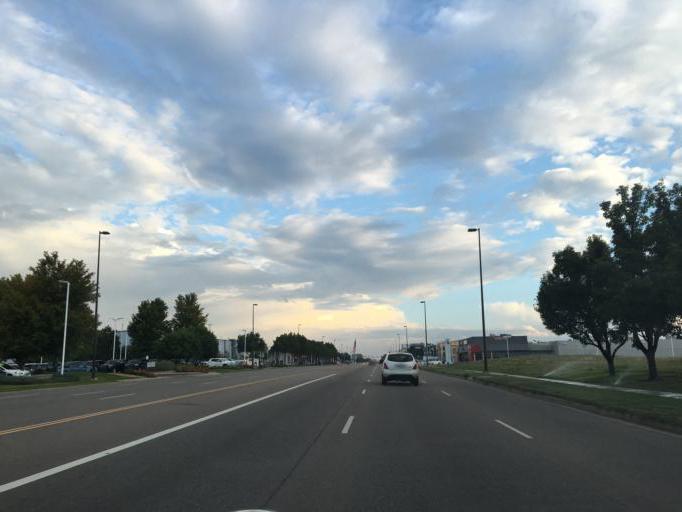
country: US
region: Colorado
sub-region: Adams County
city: Aurora
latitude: 39.7089
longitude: -104.8661
